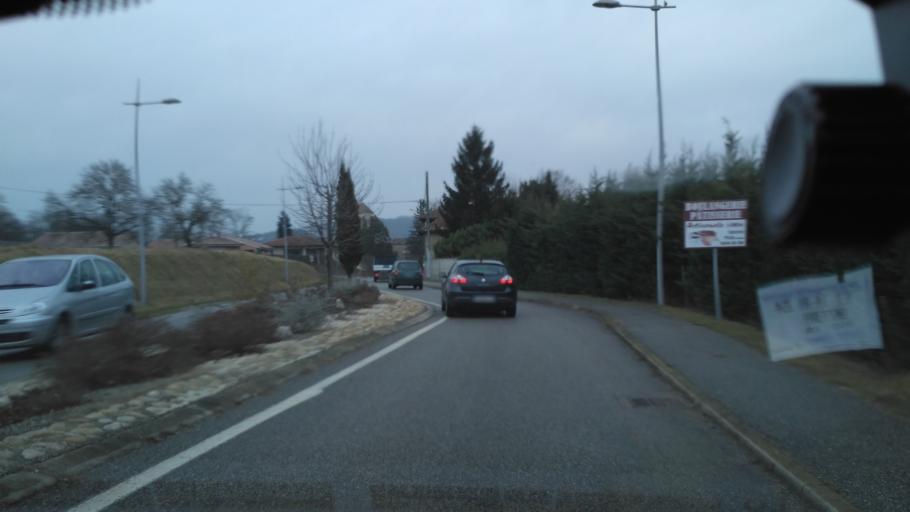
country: FR
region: Rhone-Alpes
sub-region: Departement de la Drome
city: Genissieux
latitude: 45.1425
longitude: 5.1192
